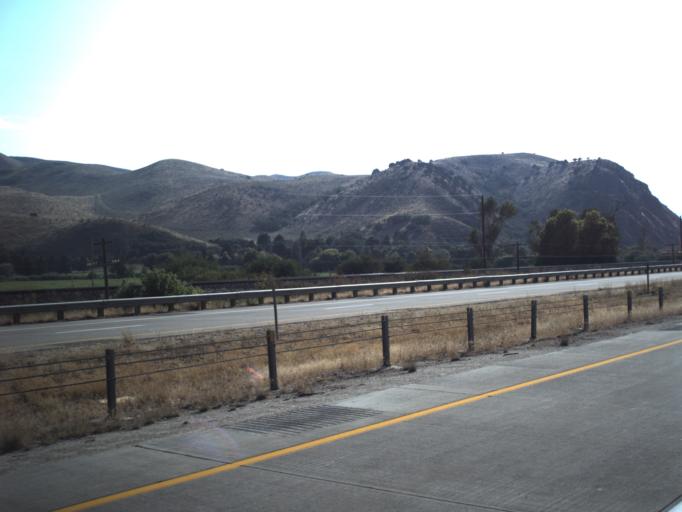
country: US
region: Utah
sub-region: Morgan County
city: Morgan
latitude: 41.0490
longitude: -111.6374
